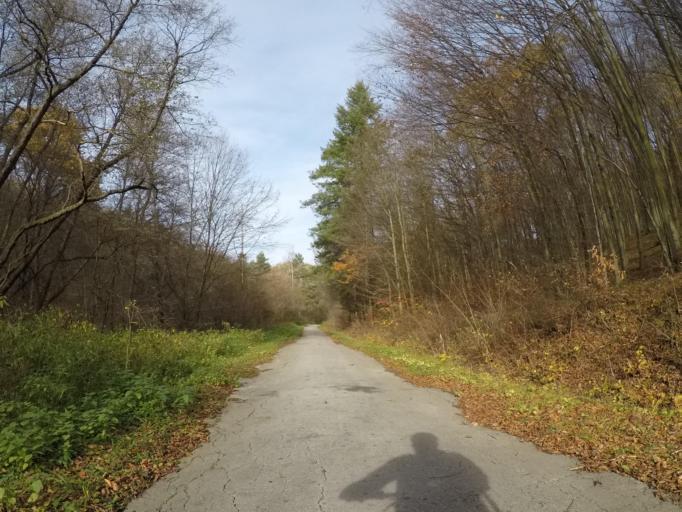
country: SK
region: Presovsky
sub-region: Okres Presov
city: Presov
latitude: 48.9613
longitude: 21.1932
